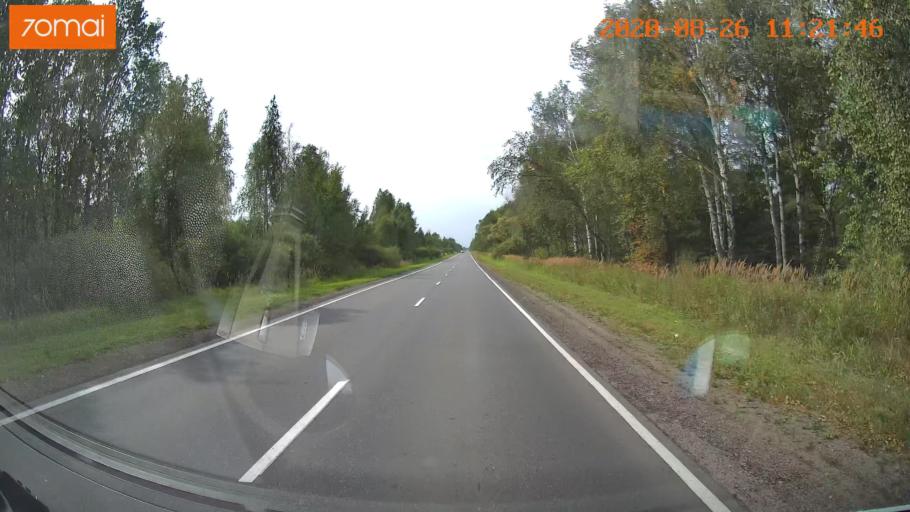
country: RU
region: Rjazan
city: Shilovo
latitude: 54.3723
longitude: 41.0391
